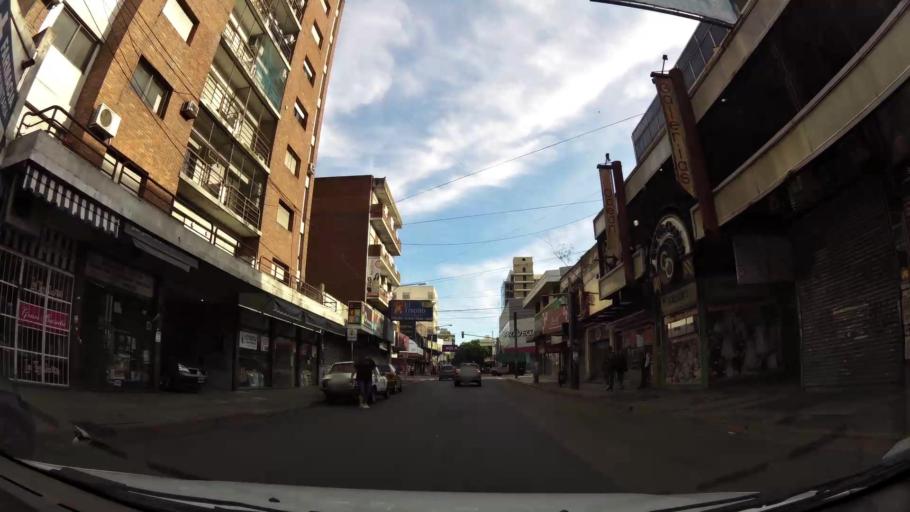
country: AR
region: Buenos Aires
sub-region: Partido de Moron
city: Moron
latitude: -34.6500
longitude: -58.6186
